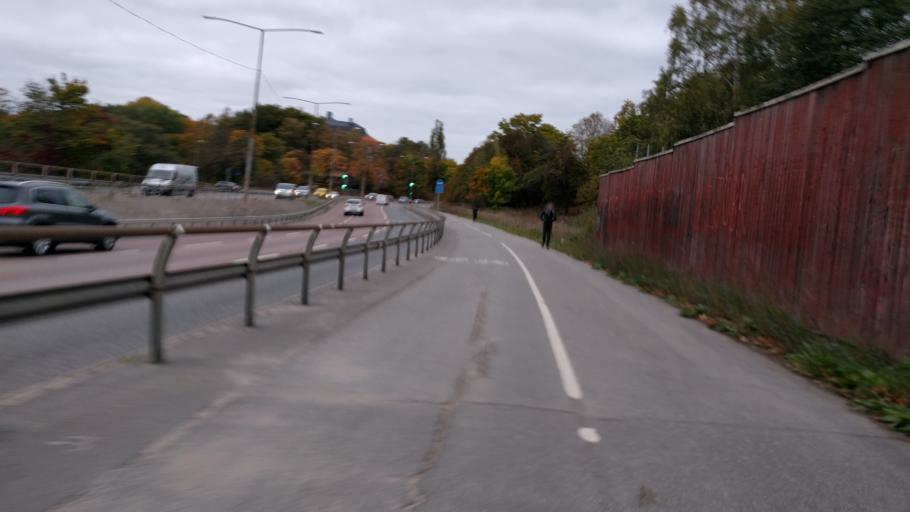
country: SE
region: Stockholm
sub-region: Stockholms Kommun
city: Stockholm
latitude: 59.3586
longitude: 18.0570
